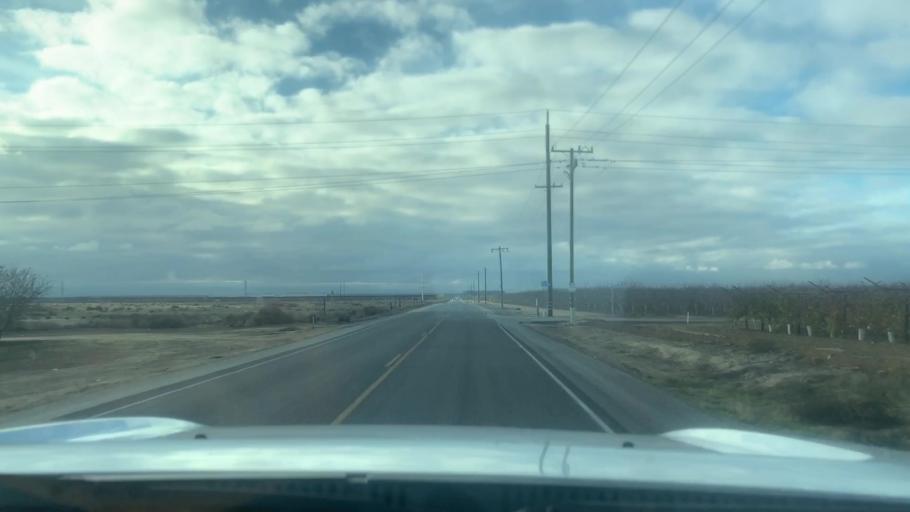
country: US
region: California
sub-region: Kern County
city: Buttonwillow
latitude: 35.5006
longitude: -119.4388
